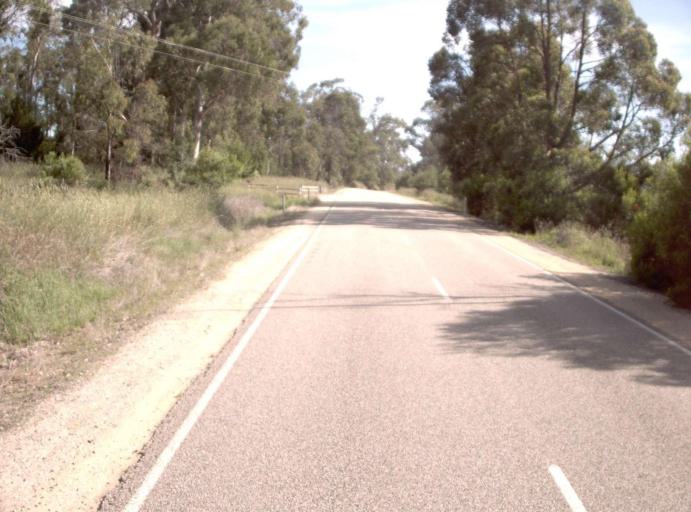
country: AU
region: Victoria
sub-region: East Gippsland
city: Lakes Entrance
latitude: -37.5317
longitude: 148.1532
